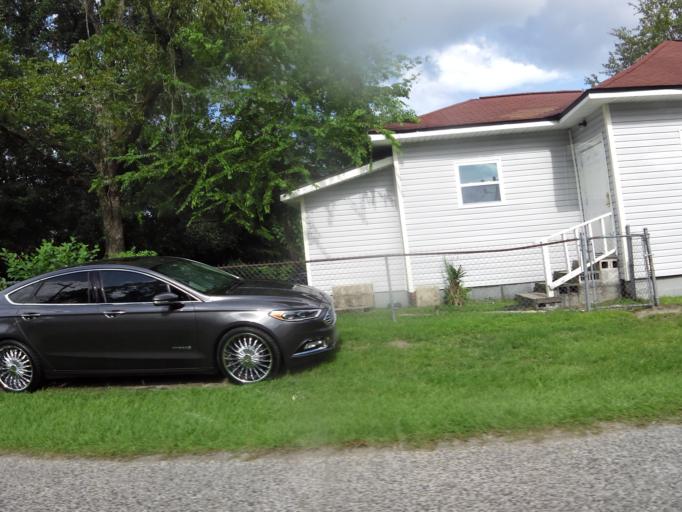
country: US
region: Florida
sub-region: Duval County
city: Jacksonville
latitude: 30.3576
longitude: -81.6830
